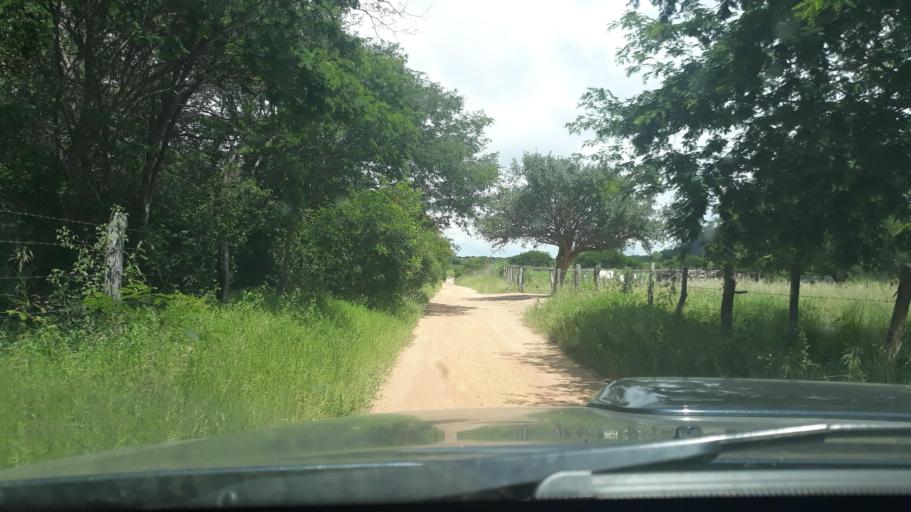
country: BR
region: Bahia
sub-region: Riacho De Santana
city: Riacho de Santana
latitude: -13.8572
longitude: -43.0438
